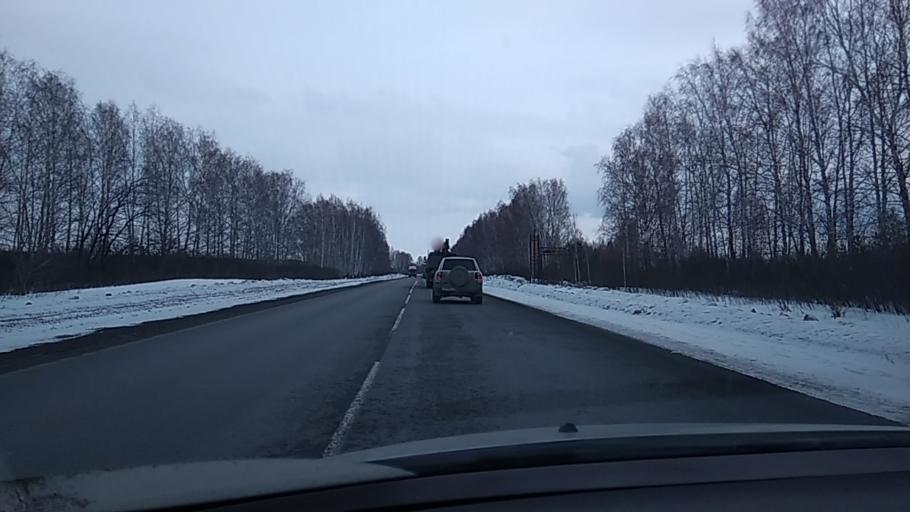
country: RU
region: Sverdlovsk
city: Sovkhoznyy
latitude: 56.5160
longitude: 61.4466
